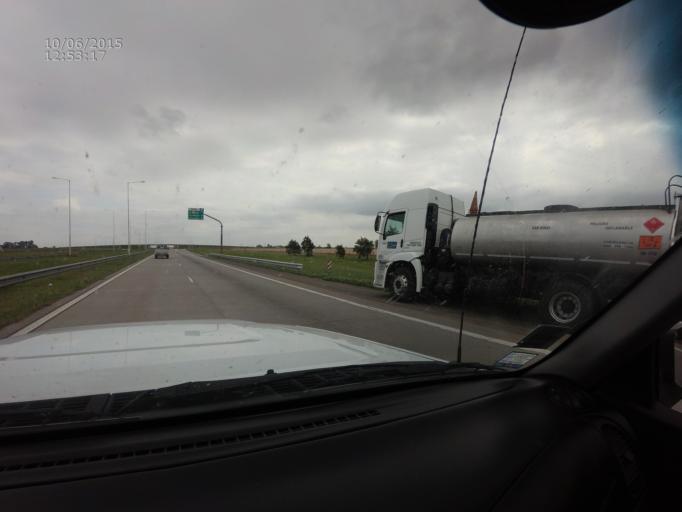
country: AR
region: Santa Fe
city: Armstrong
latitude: -32.8196
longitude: -61.5477
